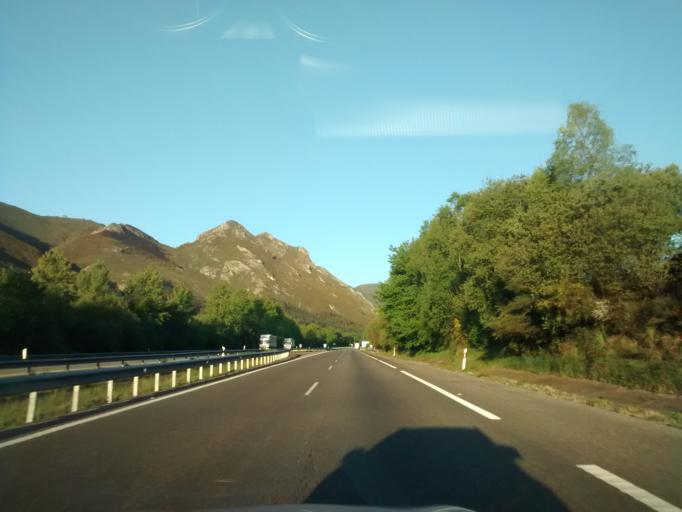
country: ES
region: Asturias
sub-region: Province of Asturias
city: Ribadesella
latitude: 43.4424
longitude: -4.9468
